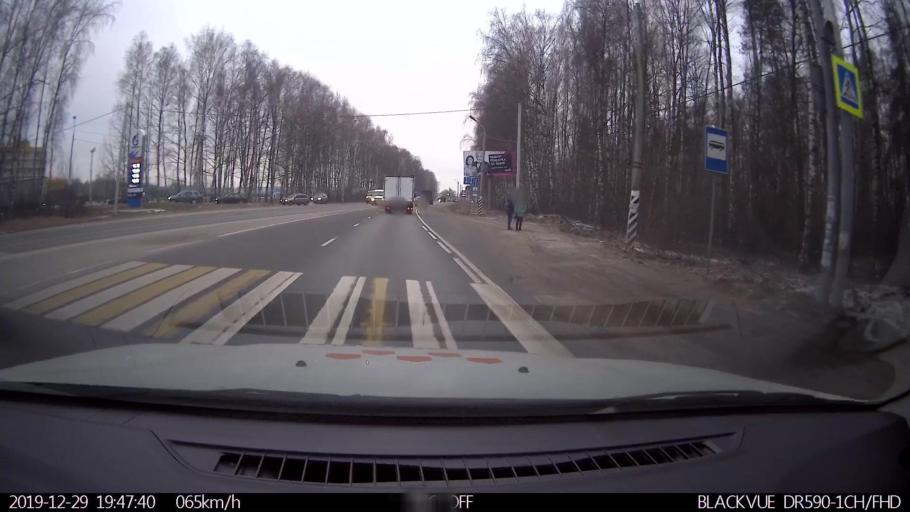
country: RU
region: Nizjnij Novgorod
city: Neklyudovo
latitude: 56.3918
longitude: 44.0103
